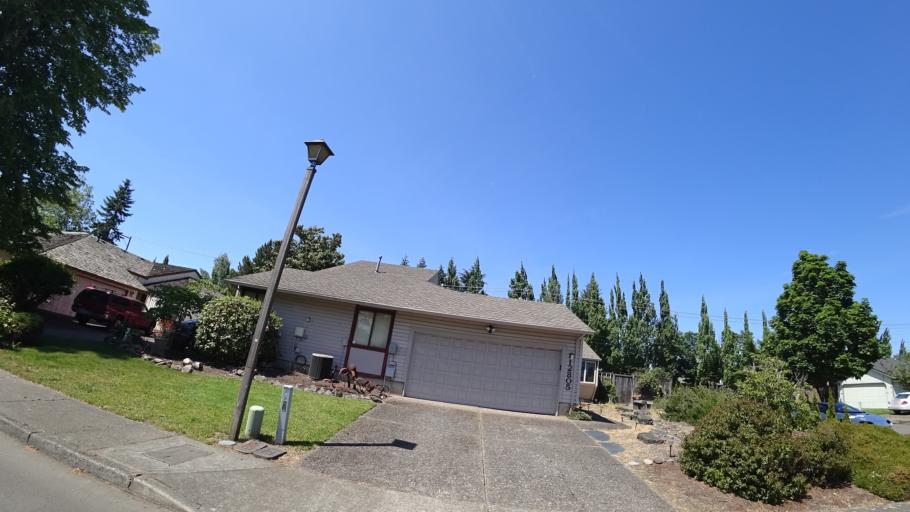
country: US
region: Oregon
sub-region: Washington County
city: Tigard
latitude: 45.4428
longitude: -122.8083
